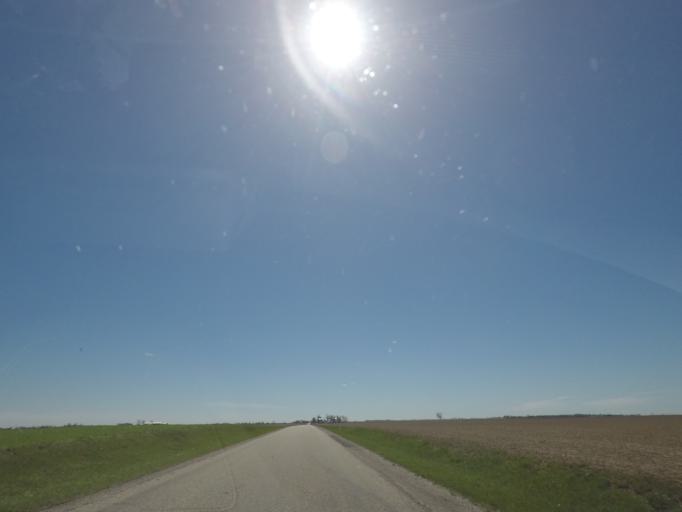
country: US
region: Illinois
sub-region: Logan County
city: Atlanta
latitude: 40.2097
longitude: -89.1944
